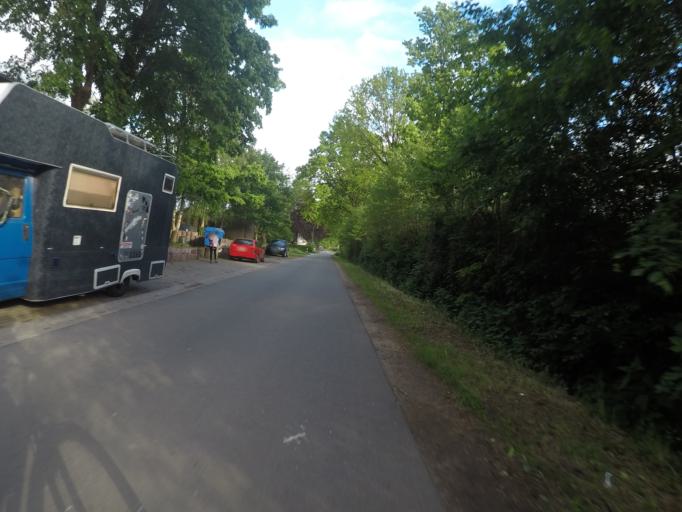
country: DE
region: Schleswig-Holstein
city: Bonningstedt
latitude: 53.6885
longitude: 9.9241
